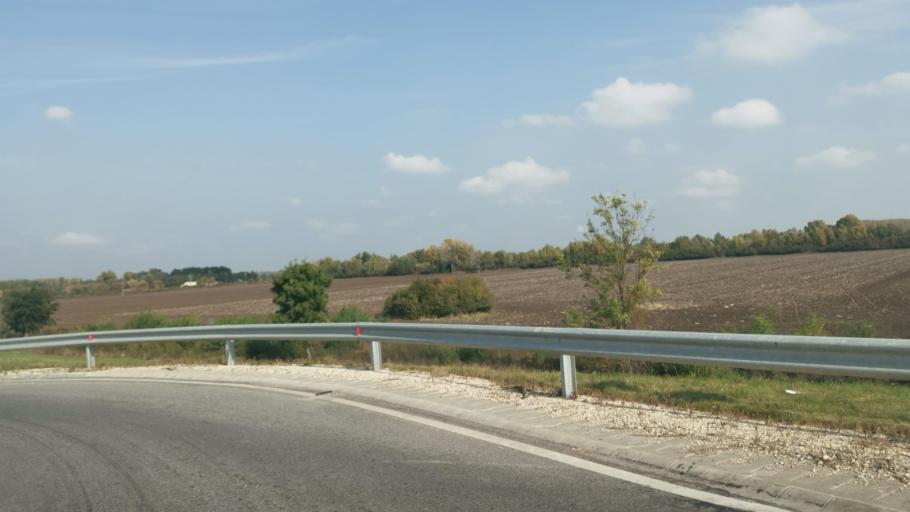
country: HU
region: Gyor-Moson-Sopron
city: Kapuvar
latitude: 47.5712
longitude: 17.0482
